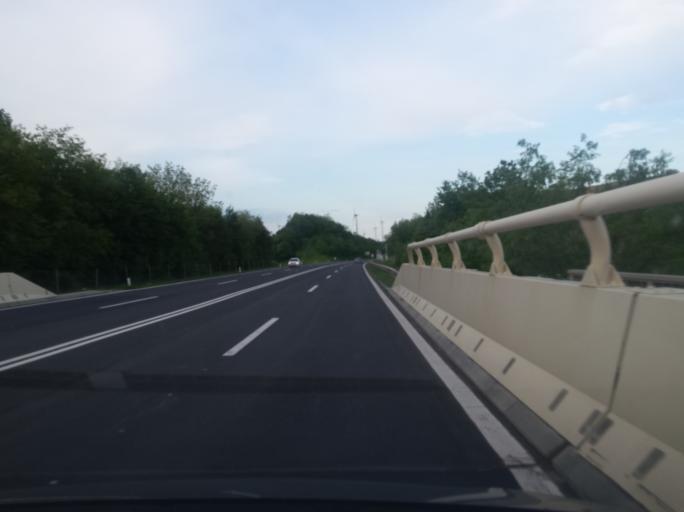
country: AT
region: Burgenland
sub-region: Politischer Bezirk Mattersburg
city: Mattersburg
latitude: 47.7492
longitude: 16.3886
